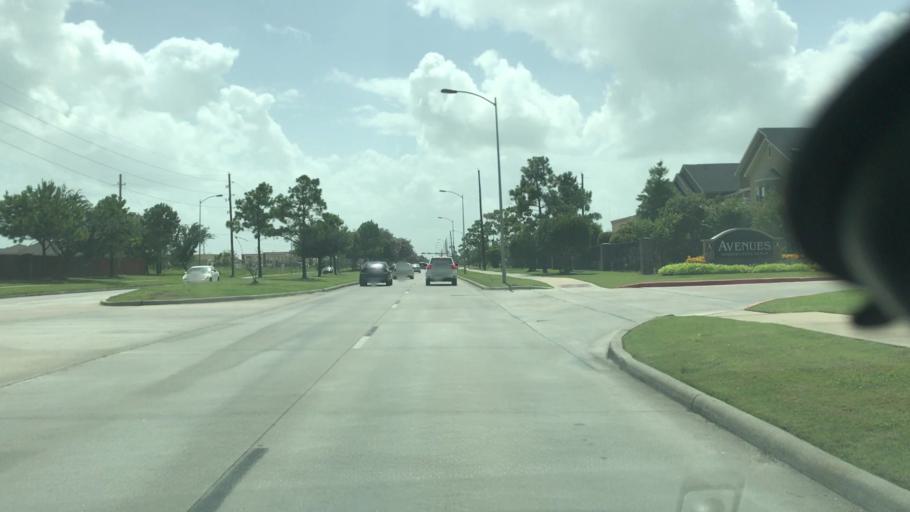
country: US
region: Texas
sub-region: Fort Bend County
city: Fresno
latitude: 29.5555
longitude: -95.4135
